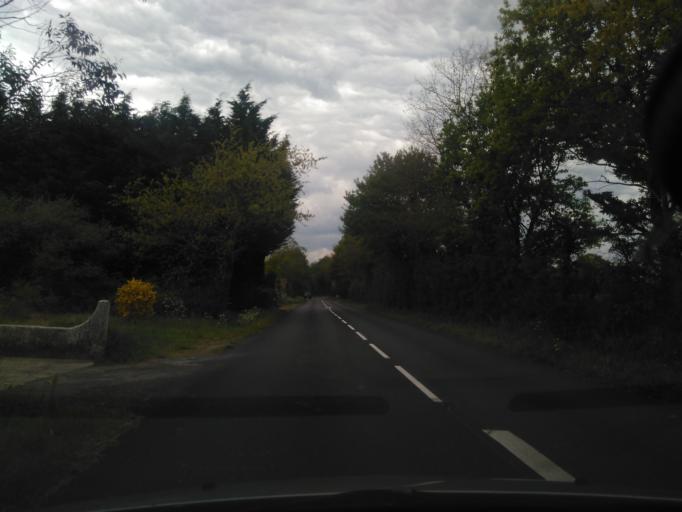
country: FR
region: Pays de la Loire
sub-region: Departement de la Vendee
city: Dompierre-sur-Yon
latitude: 46.7164
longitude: -1.4095
